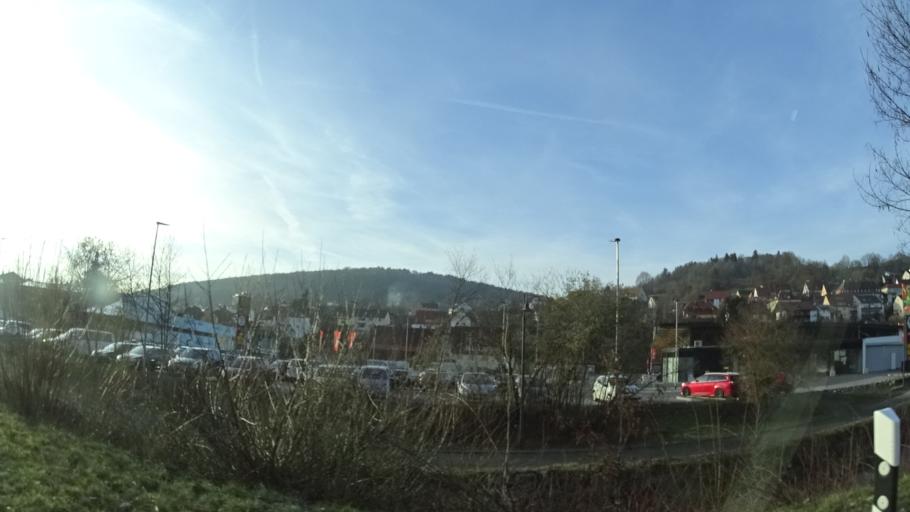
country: DE
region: Bavaria
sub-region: Regierungsbezirk Unterfranken
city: Bad Bruckenau
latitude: 50.3116
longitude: 9.7968
